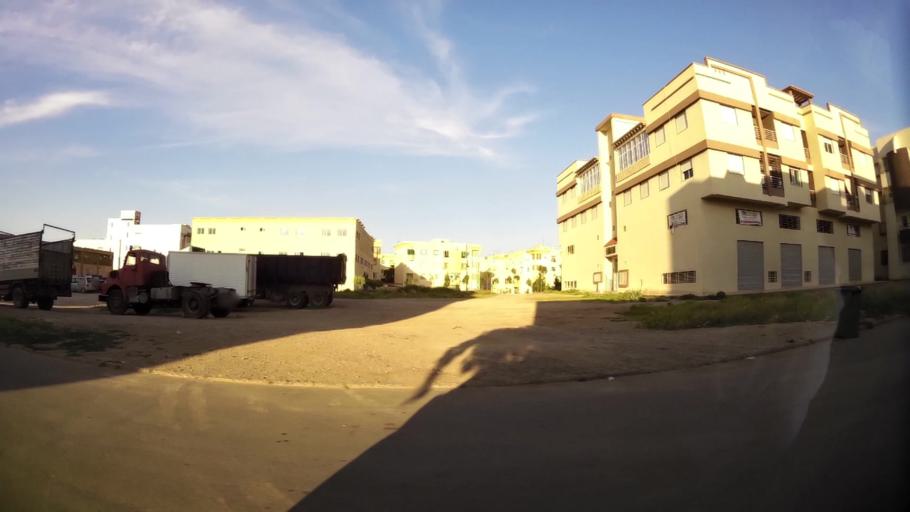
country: MA
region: Oriental
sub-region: Oujda-Angad
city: Oujda
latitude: 34.6997
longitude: -1.9163
